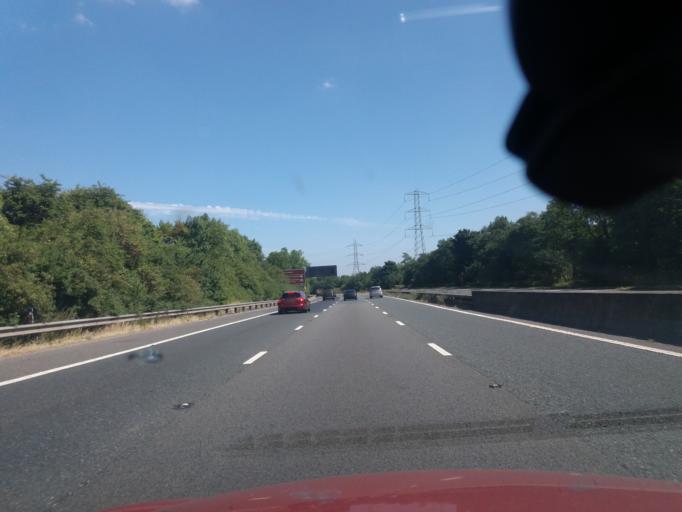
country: GB
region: England
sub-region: City and Borough of Salford
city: Little Hulton
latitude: 53.5401
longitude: -2.4164
